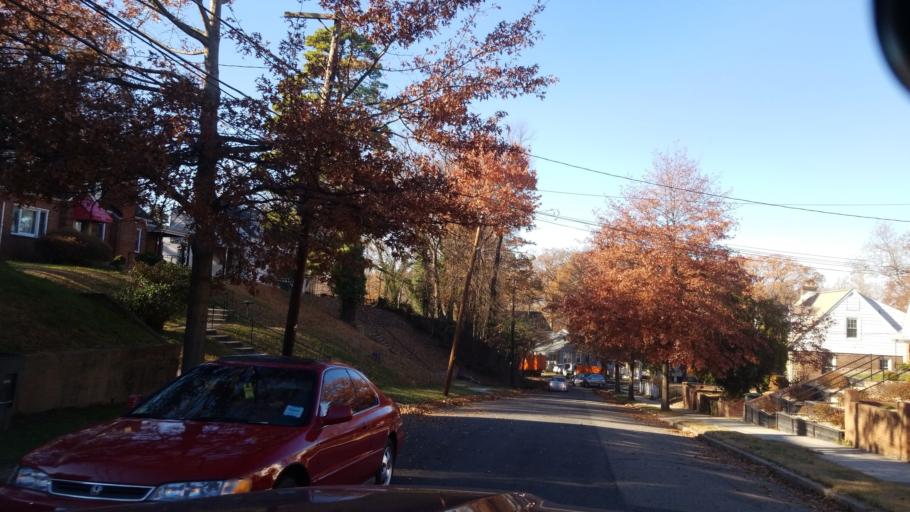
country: US
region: Maryland
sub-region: Prince George's County
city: Mount Rainier
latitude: 38.9323
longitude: -76.9620
